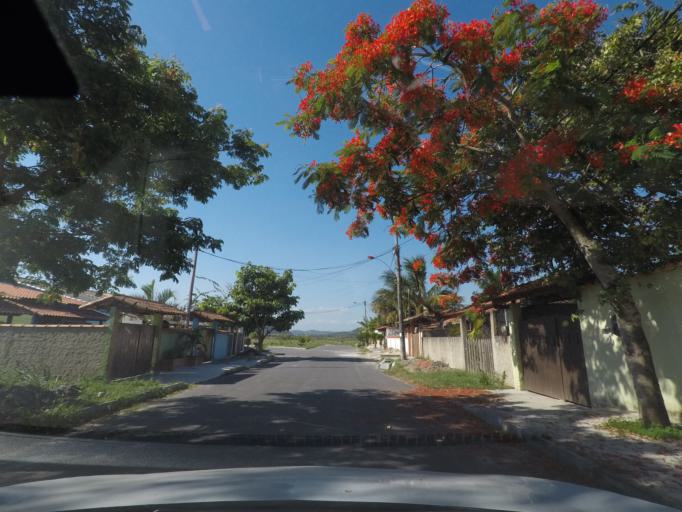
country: BR
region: Rio de Janeiro
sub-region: Marica
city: Marica
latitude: -22.9653
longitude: -42.9217
